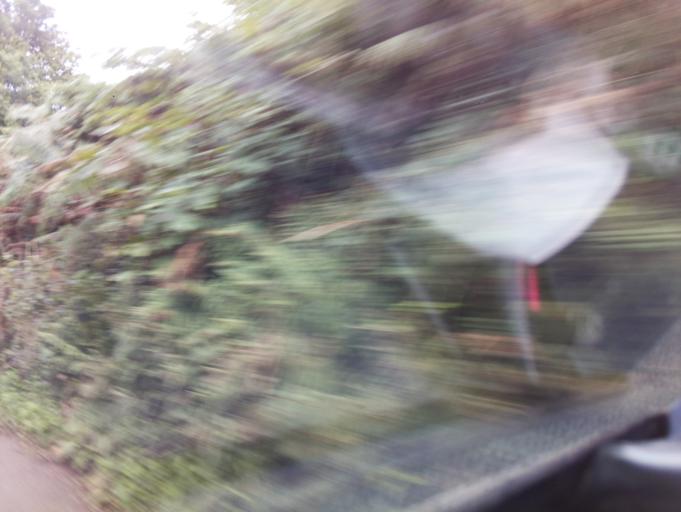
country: GB
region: England
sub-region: Devon
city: Dartmouth
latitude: 50.3410
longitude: -3.6305
